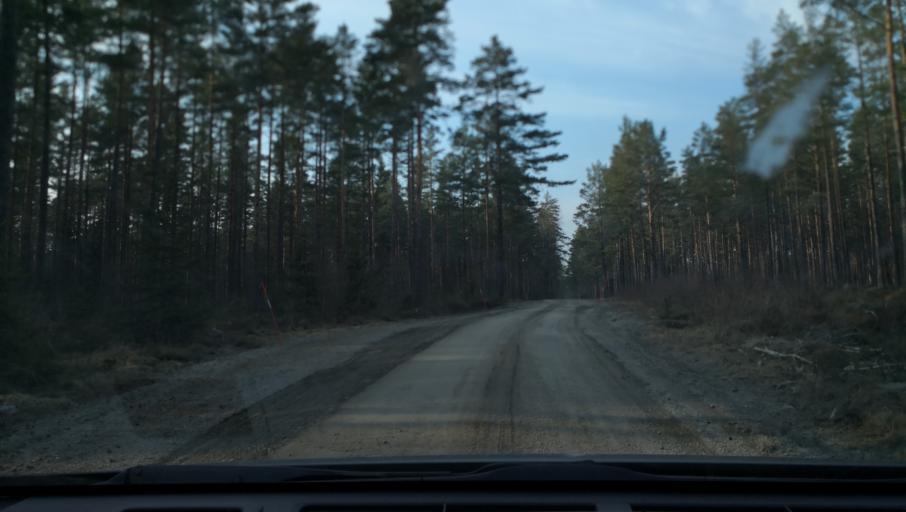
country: SE
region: OErebro
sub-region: Lindesbergs Kommun
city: Frovi
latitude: 59.3639
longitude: 15.3278
